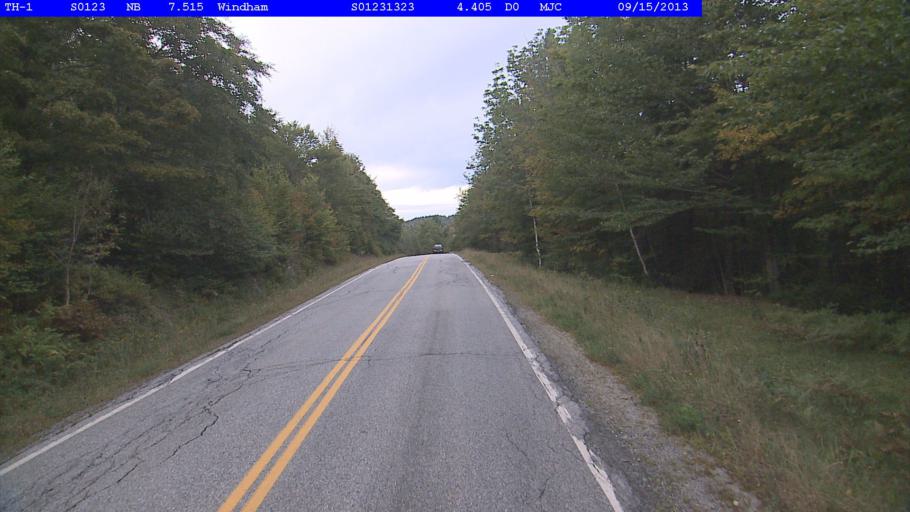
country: US
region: Vermont
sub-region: Windsor County
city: Chester
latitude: 43.1868
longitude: -72.7210
